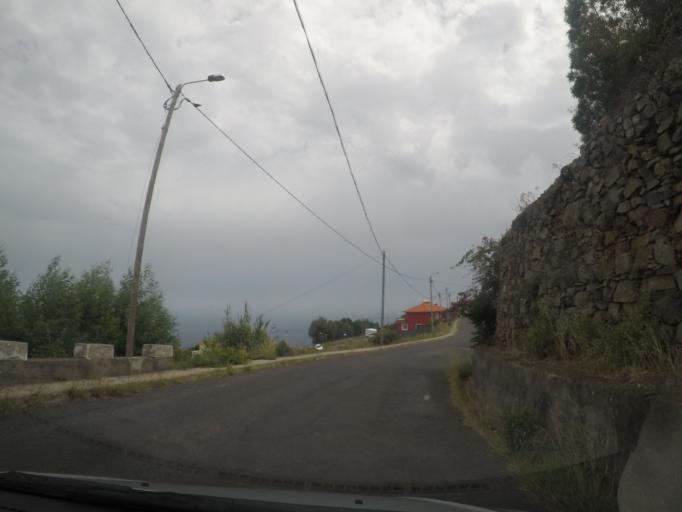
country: PT
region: Madeira
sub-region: Santa Cruz
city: Santa Cruz
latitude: 32.6782
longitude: -16.8093
